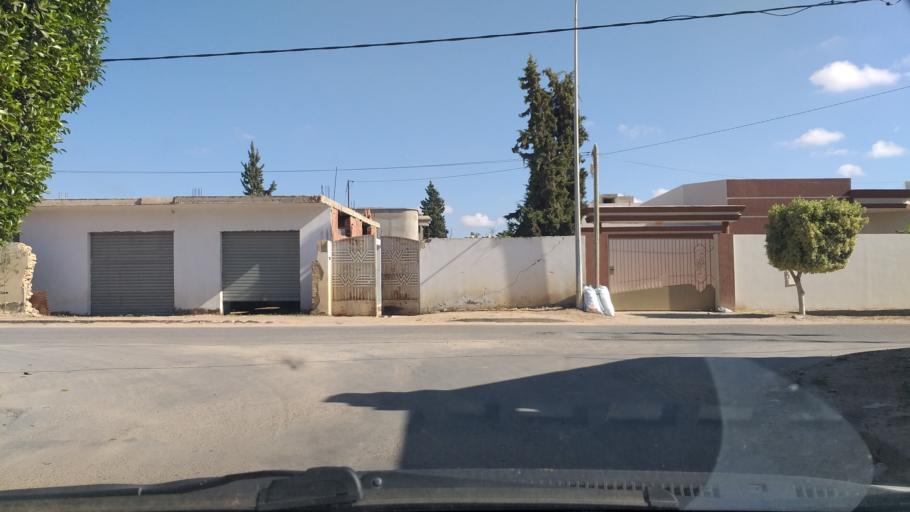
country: TN
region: Safaqis
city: Al Qarmadah
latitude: 34.8043
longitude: 10.7692
